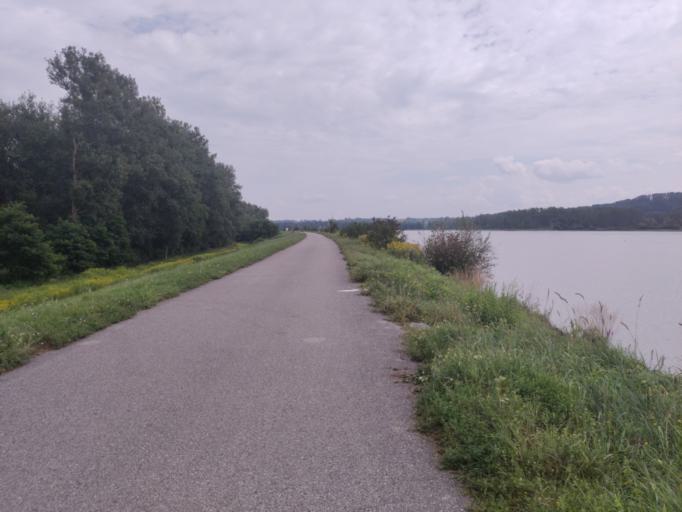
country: AT
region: Lower Austria
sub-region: Politischer Bezirk Amstetten
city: Strengberg
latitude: 48.1692
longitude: 14.6604
